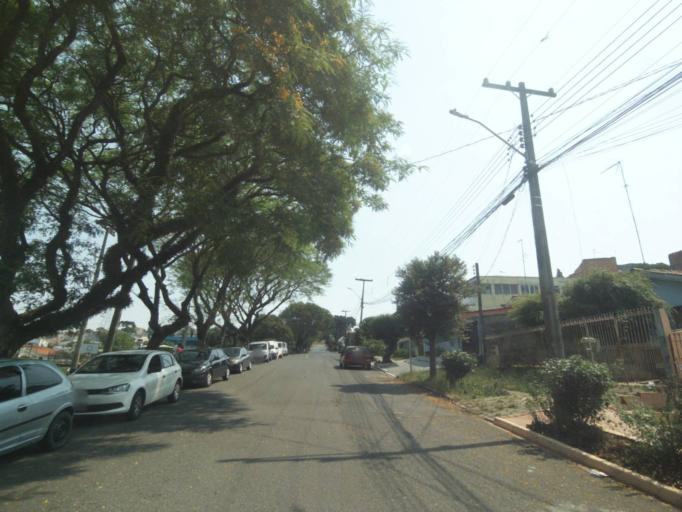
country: BR
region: Parana
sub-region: Sao Jose Dos Pinhais
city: Sao Jose dos Pinhais
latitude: -25.5323
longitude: -49.2507
